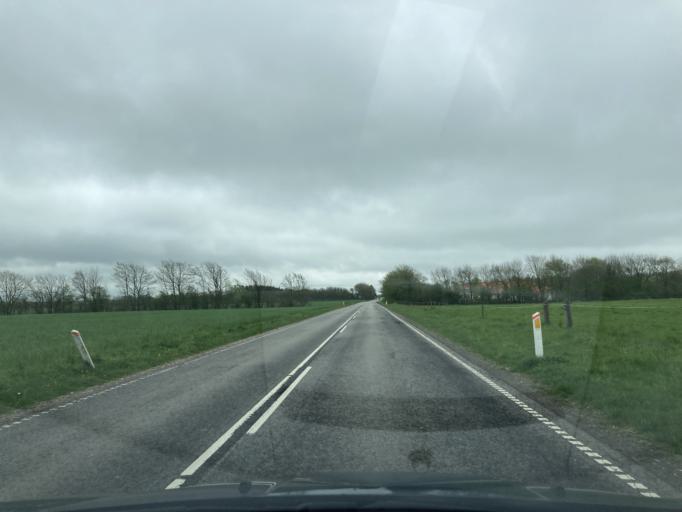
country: DK
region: North Denmark
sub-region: Thisted Kommune
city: Hurup
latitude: 56.8506
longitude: 8.3673
